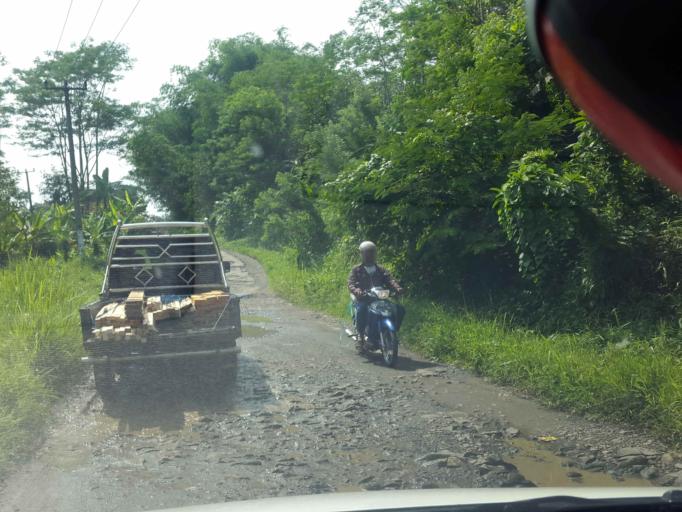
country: ID
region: West Java
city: Pasirreungit
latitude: -6.9311
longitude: 107.0066
